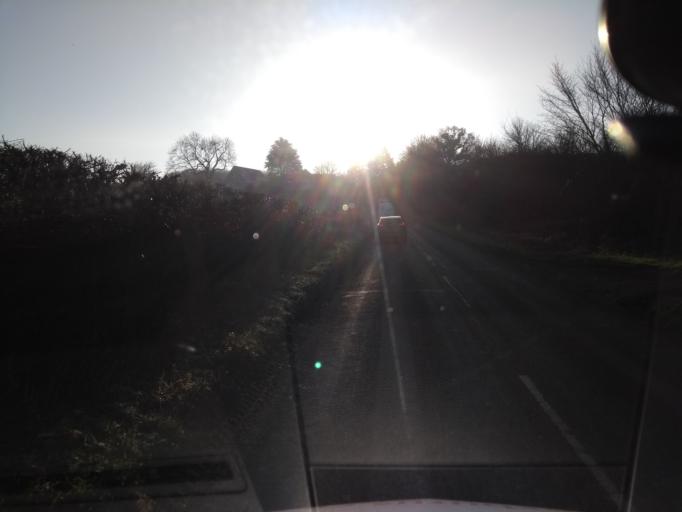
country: GB
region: England
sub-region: Somerset
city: Evercreech
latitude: 51.1346
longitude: -2.4808
